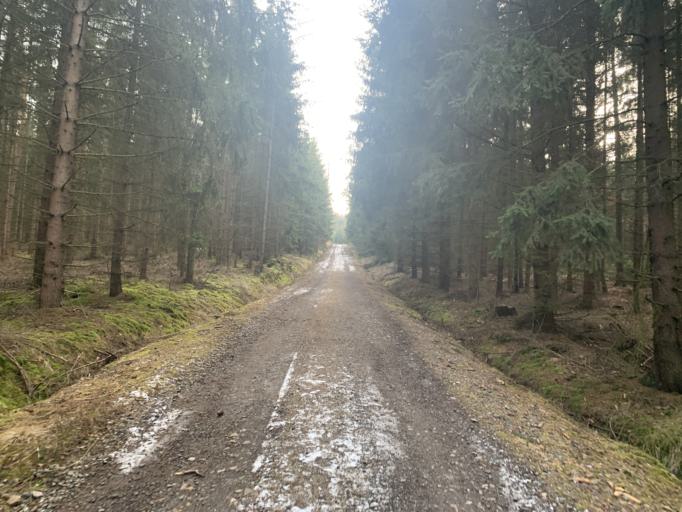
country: CZ
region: Plzensky
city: Zbiroh
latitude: 49.8238
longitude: 13.7973
